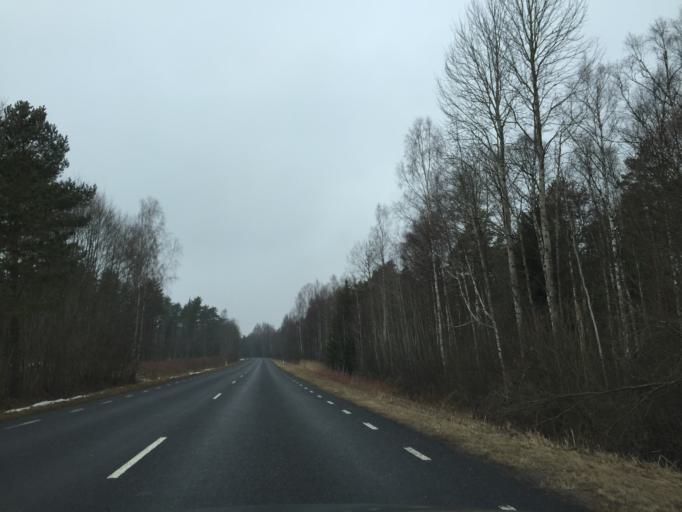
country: EE
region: Laeaene
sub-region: Lihula vald
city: Lihula
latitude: 58.5605
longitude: 23.8312
